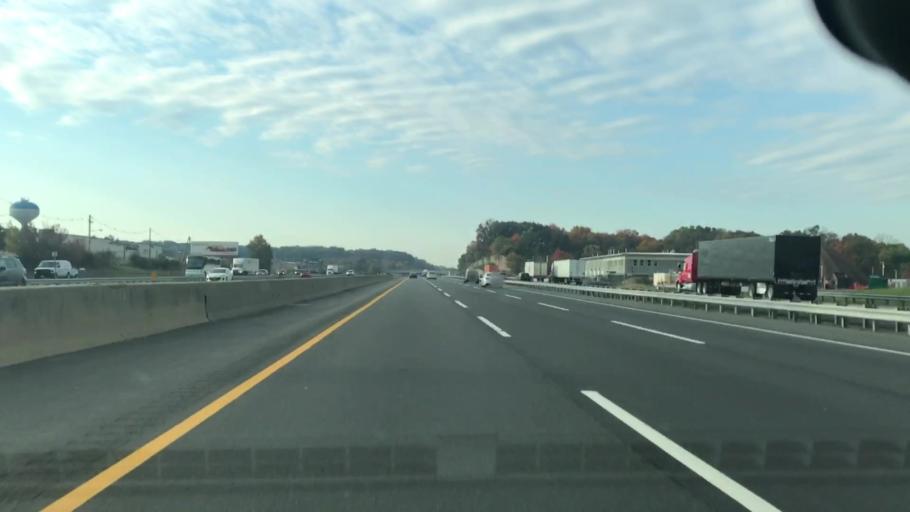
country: US
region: New Jersey
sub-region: Middlesex County
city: Milltown
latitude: 40.4465
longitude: -74.4251
